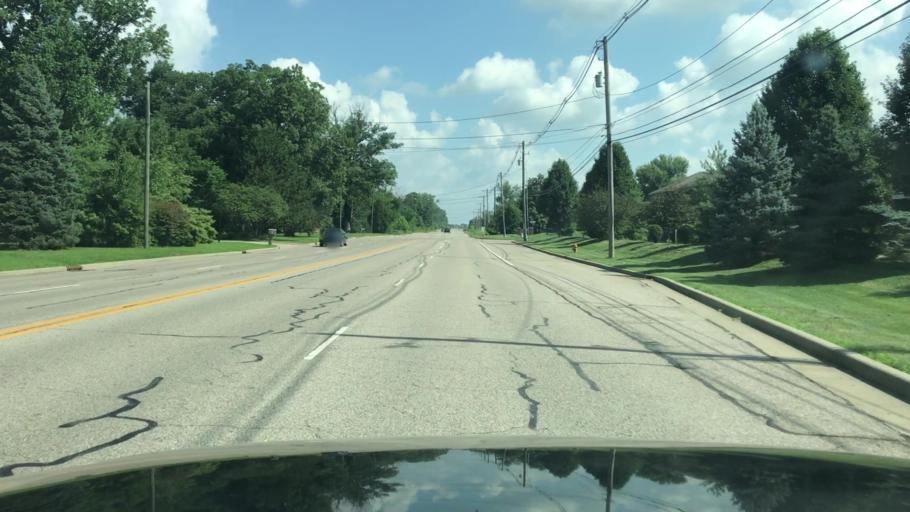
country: US
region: Indiana
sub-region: Vanderburgh County
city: Melody Hill
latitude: 38.0155
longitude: -87.4922
